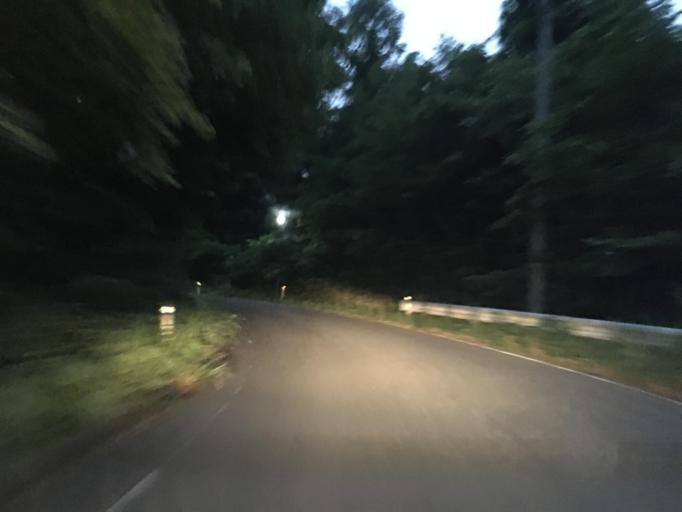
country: JP
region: Miyagi
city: Furukawa
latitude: 38.7686
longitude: 140.9095
